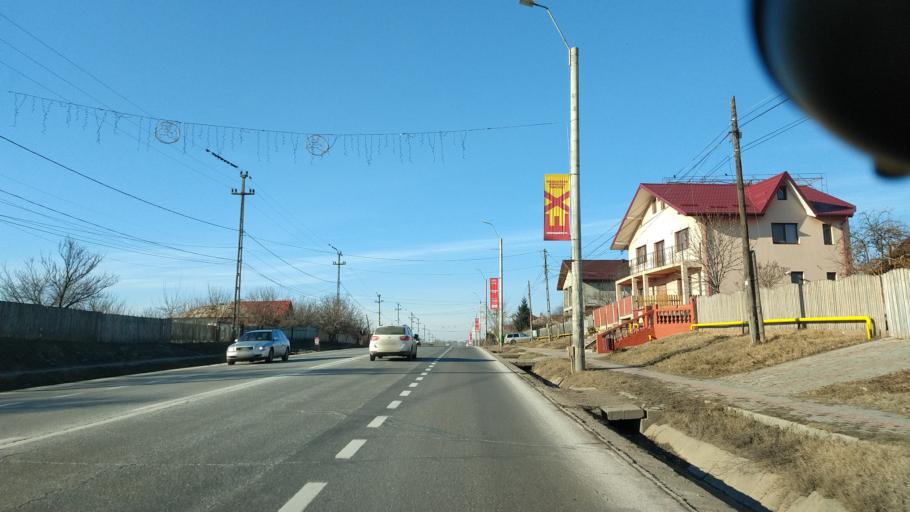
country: RO
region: Iasi
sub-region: Comuna Letcani
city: Letcani
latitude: 47.1922
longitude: 27.4247
